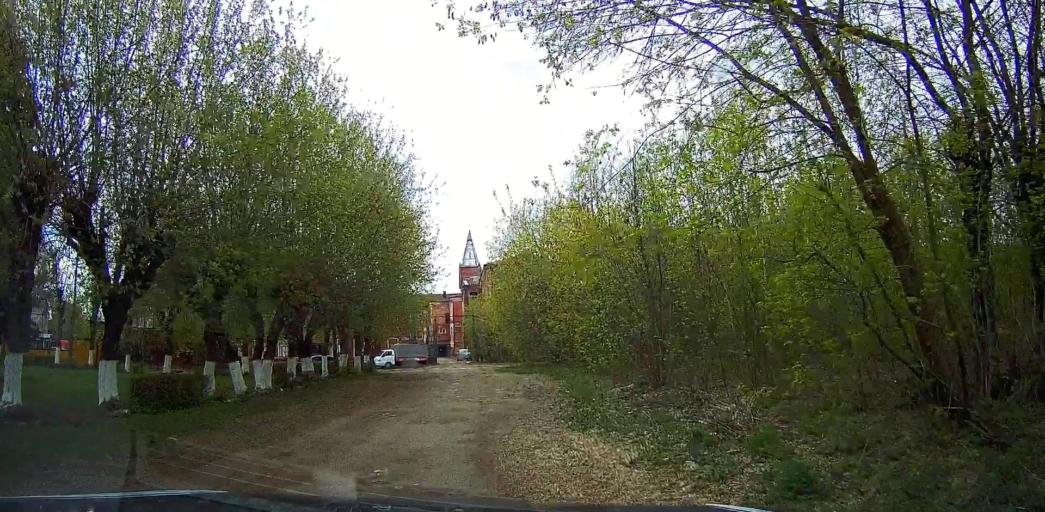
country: RU
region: Moskovskaya
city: Pavlovskiy Posad
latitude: 55.7855
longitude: 38.6869
